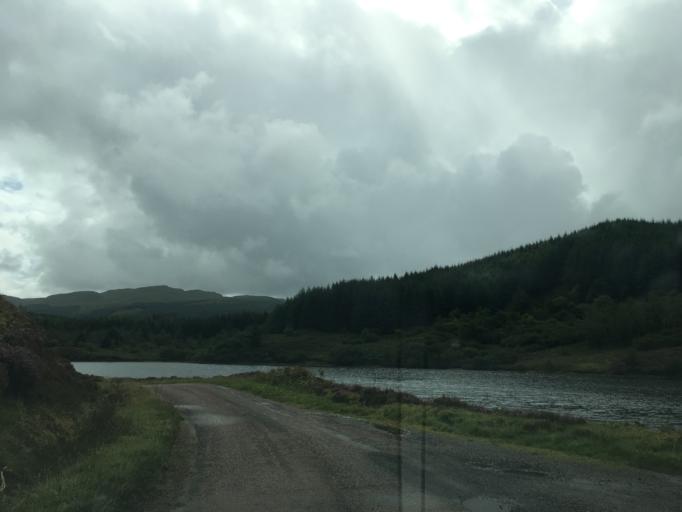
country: GB
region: Scotland
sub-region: Argyll and Bute
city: Oban
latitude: 56.2529
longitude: -5.4420
